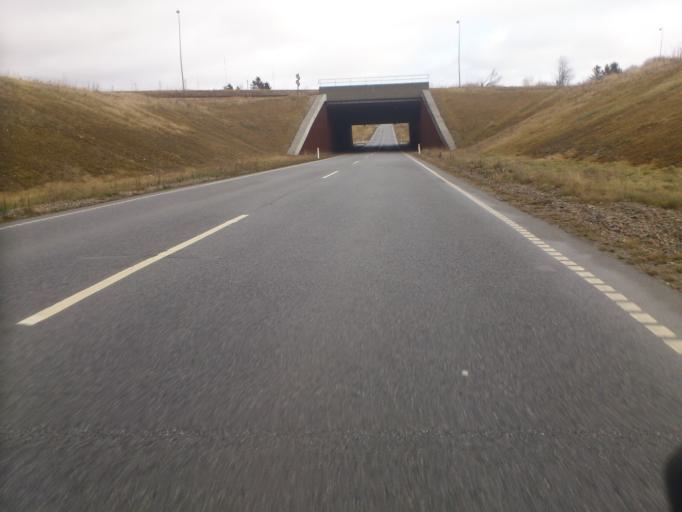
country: DK
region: South Denmark
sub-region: Fredericia Kommune
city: Fredericia
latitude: 55.5877
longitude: 9.7094
